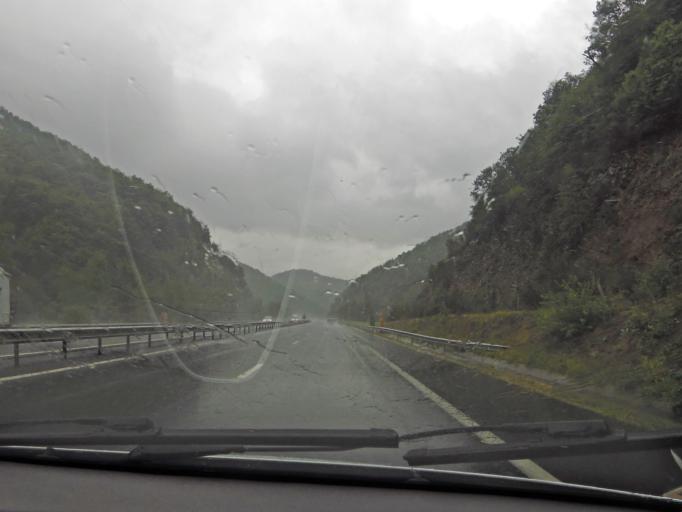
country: FR
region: Auvergne
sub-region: Departement du Cantal
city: Massiac
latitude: 45.2063
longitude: 3.1979
